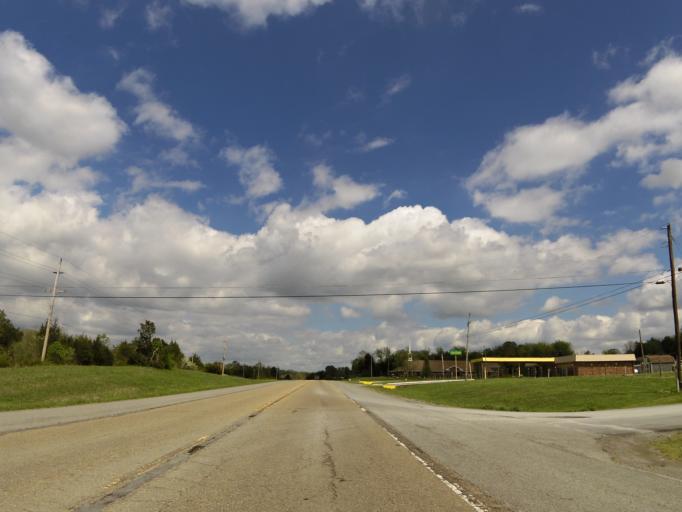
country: US
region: Tennessee
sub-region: Claiborne County
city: Harrogate
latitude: 36.5311
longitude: -83.7078
